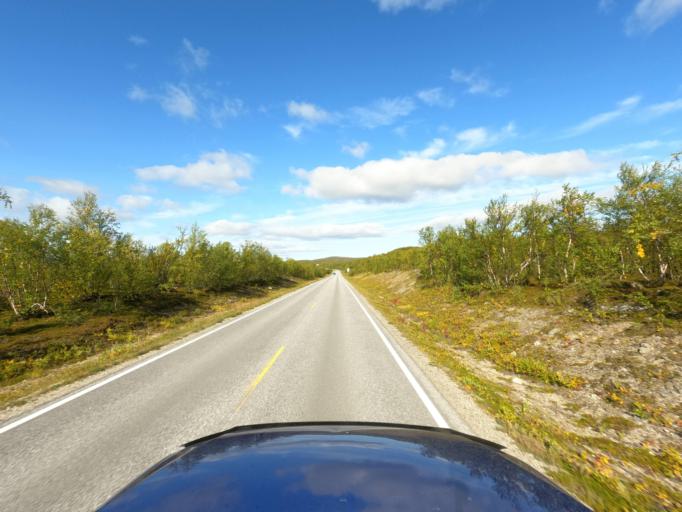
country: NO
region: Finnmark Fylke
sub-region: Karasjok
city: Karasjohka
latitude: 69.5359
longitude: 25.4333
